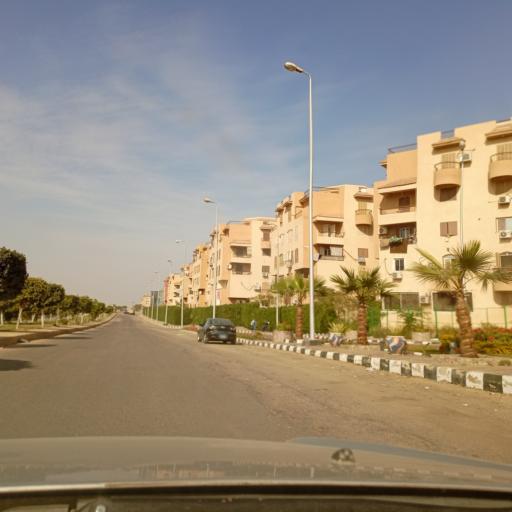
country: EG
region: Muhafazat al Qalyubiyah
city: Al Khankah
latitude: 30.0426
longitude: 31.4852
